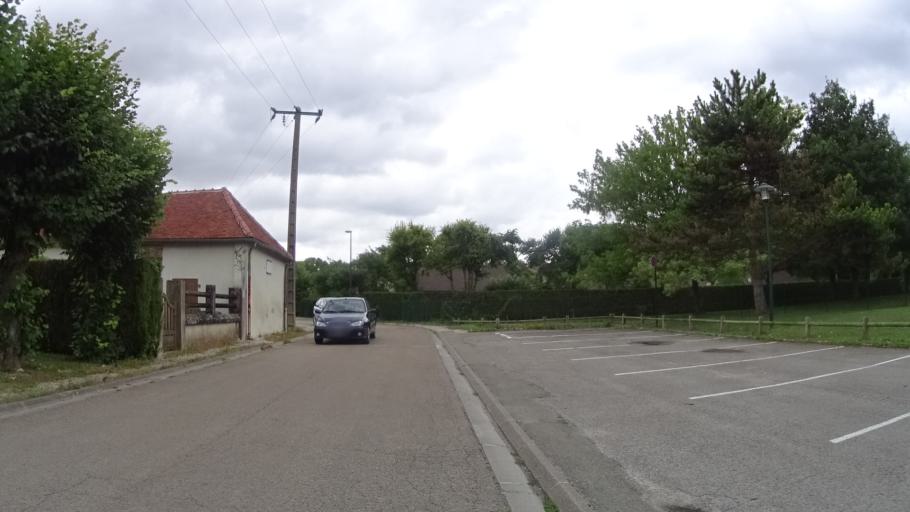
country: FR
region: Champagne-Ardenne
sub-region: Departement de l'Aube
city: Verrieres
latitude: 48.2321
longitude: 4.1496
